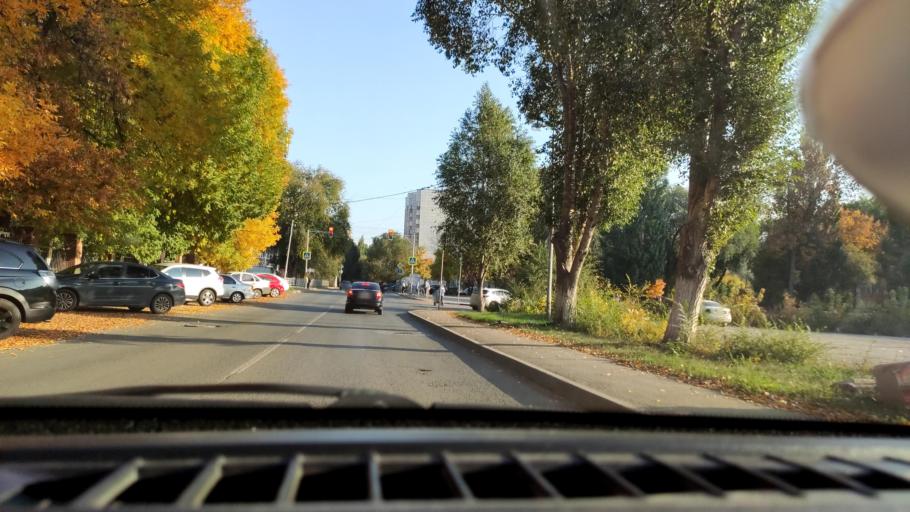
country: RU
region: Samara
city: Petra-Dubrava
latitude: 53.2346
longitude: 50.2651
